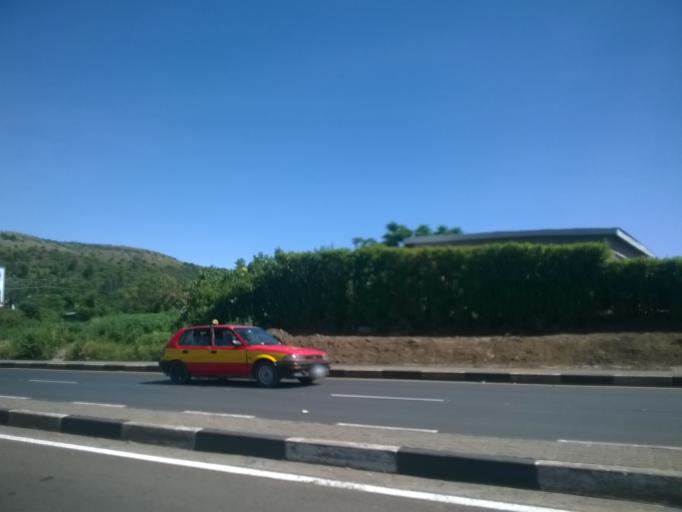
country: LS
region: Maseru
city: Maseru
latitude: -29.3005
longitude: 27.4592
